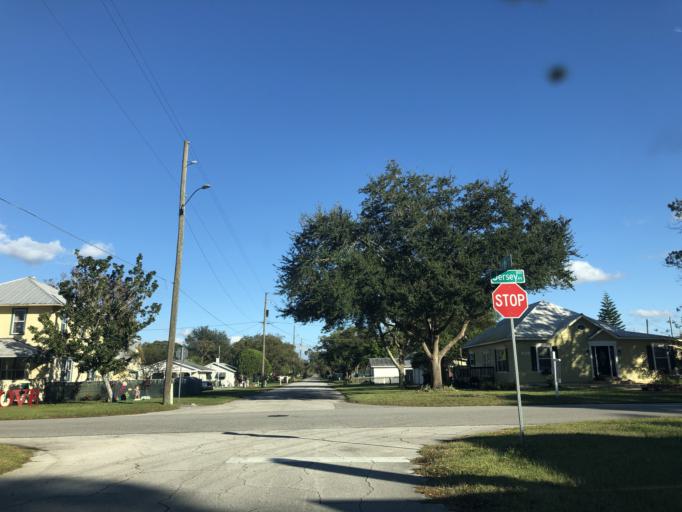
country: US
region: Florida
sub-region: Osceola County
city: Saint Cloud
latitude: 28.2506
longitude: -81.2918
